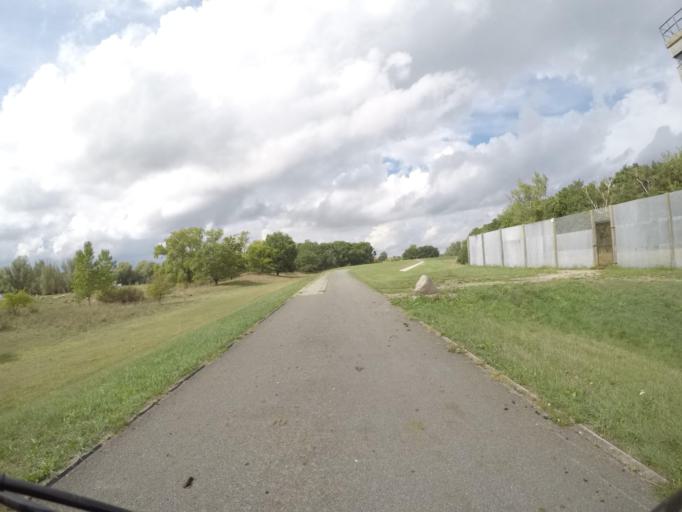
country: DE
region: Lower Saxony
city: Neu Darchau
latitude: 53.2448
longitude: 10.8794
